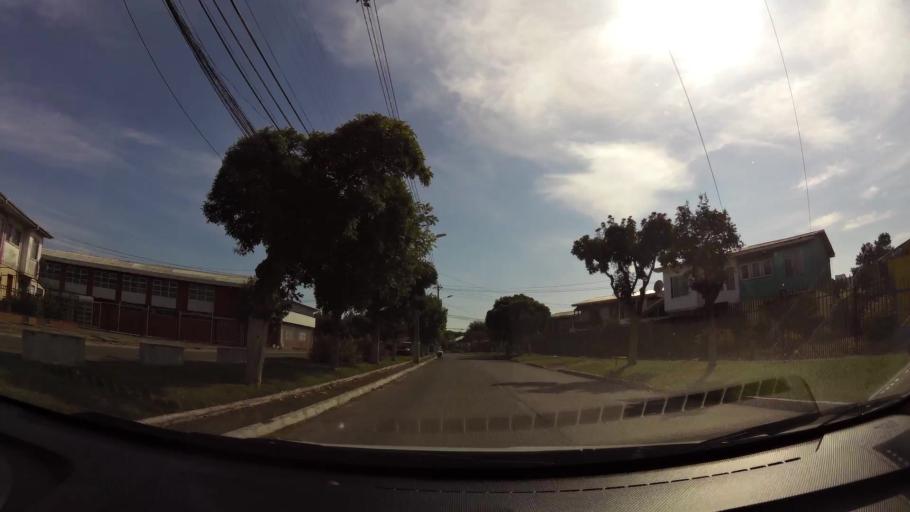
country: CL
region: Biobio
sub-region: Provincia de Concepcion
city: Talcahuano
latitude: -36.7875
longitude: -73.1069
